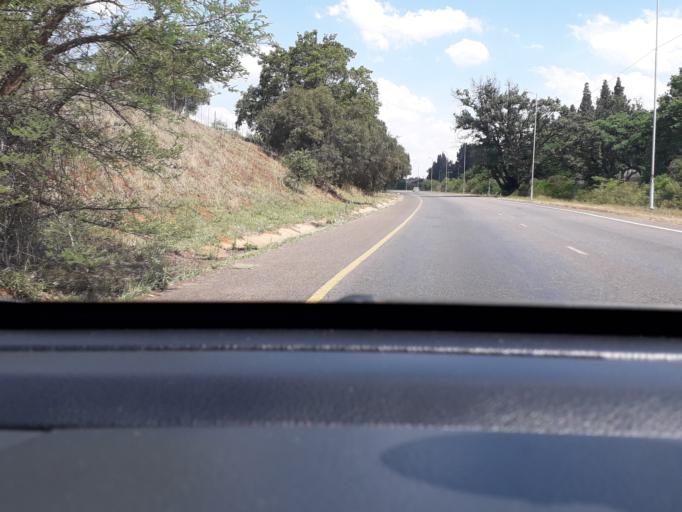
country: ZA
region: Gauteng
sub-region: City of Tshwane Metropolitan Municipality
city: Pretoria
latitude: -25.7962
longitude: 28.1965
